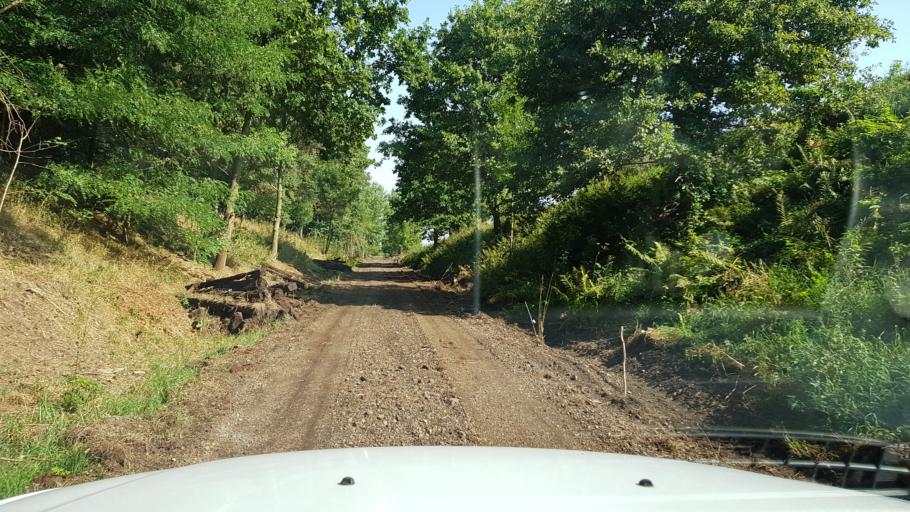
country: PL
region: West Pomeranian Voivodeship
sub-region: Powiat choszczenski
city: Pelczyce
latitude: 53.0714
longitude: 15.3095
